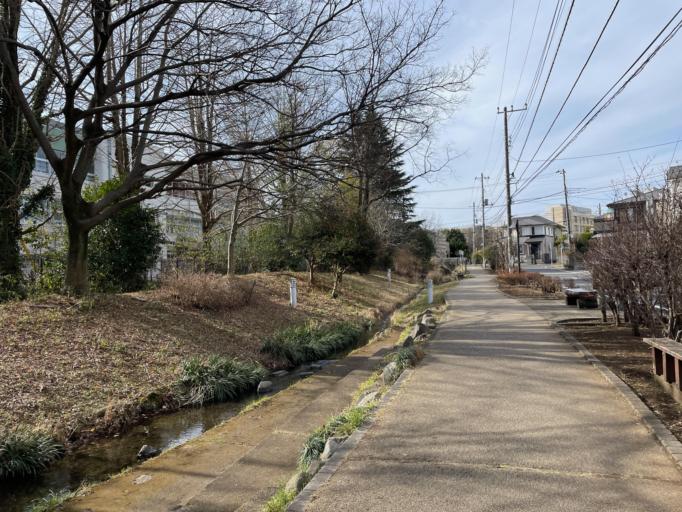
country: JP
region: Saitama
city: Tokorozawa
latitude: 35.7831
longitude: 139.5095
